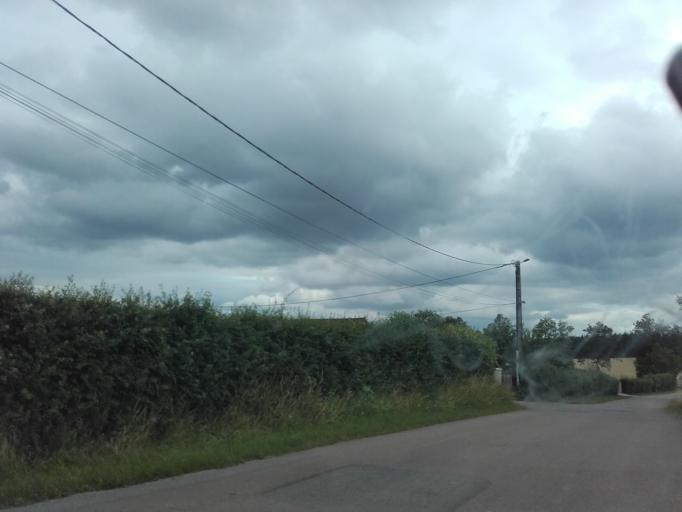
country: FR
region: Bourgogne
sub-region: Departement de Saone-et-Loire
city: Saint-Leger-sur-Dheune
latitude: 46.8865
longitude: 4.6482
